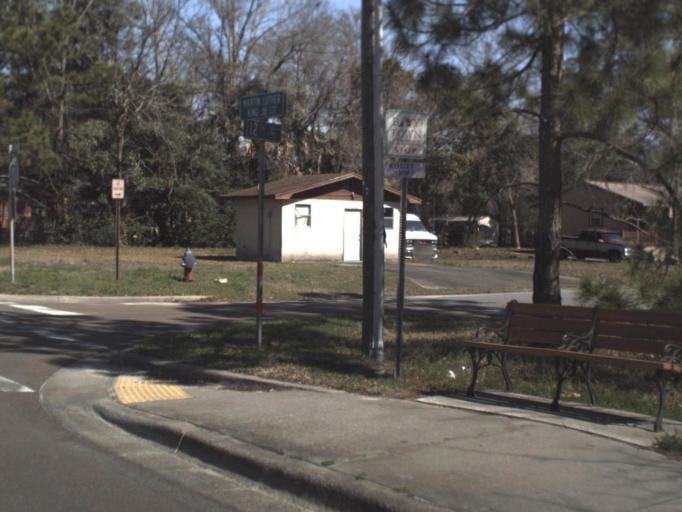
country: US
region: Florida
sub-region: Bay County
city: Panama City
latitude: 30.1695
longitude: -85.6502
